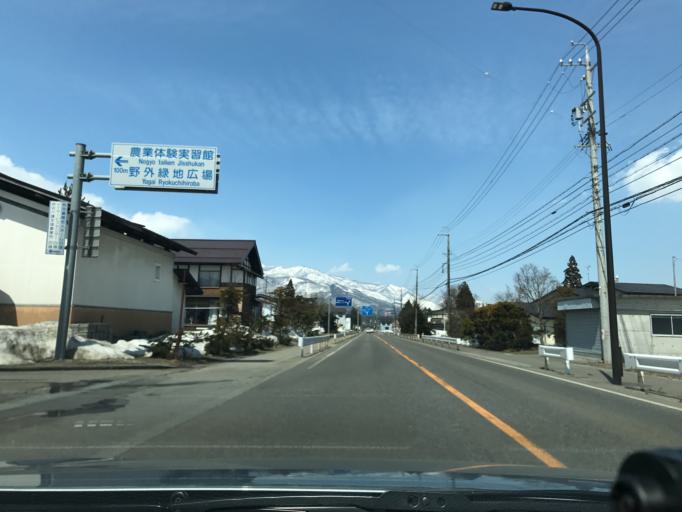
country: JP
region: Nagano
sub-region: Kitaazumi Gun
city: Hakuba
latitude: 36.6643
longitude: 137.8490
